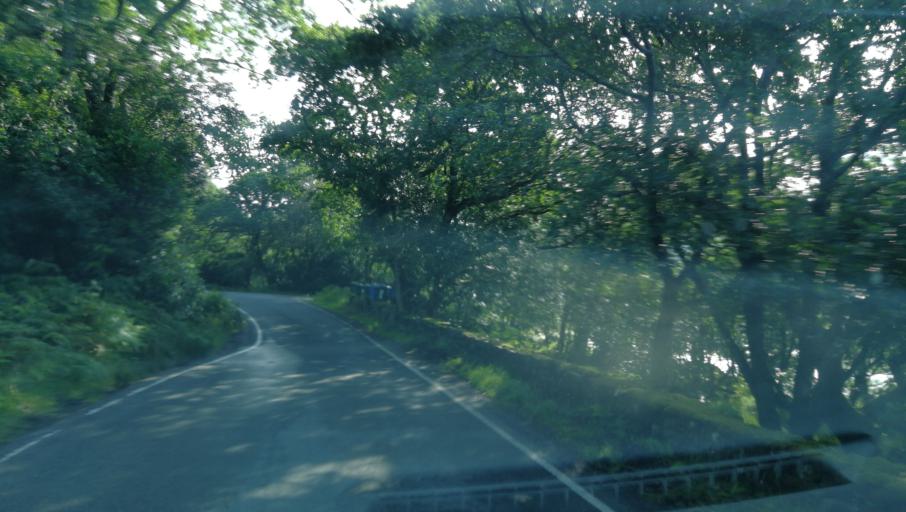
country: GB
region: Scotland
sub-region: Argyll and Bute
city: Isle Of Mull
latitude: 56.6840
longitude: -5.8229
